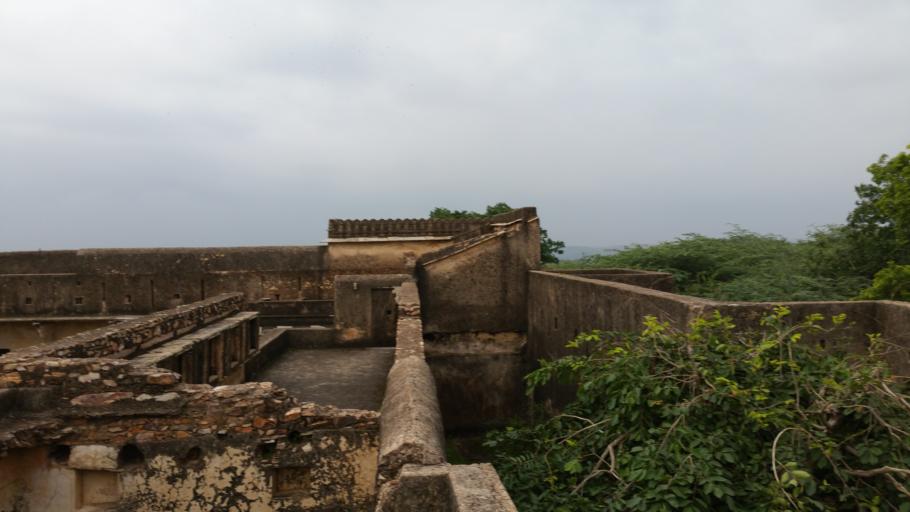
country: IN
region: Rajasthan
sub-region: Bundi
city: Bundi
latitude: 25.4517
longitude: 75.6367
